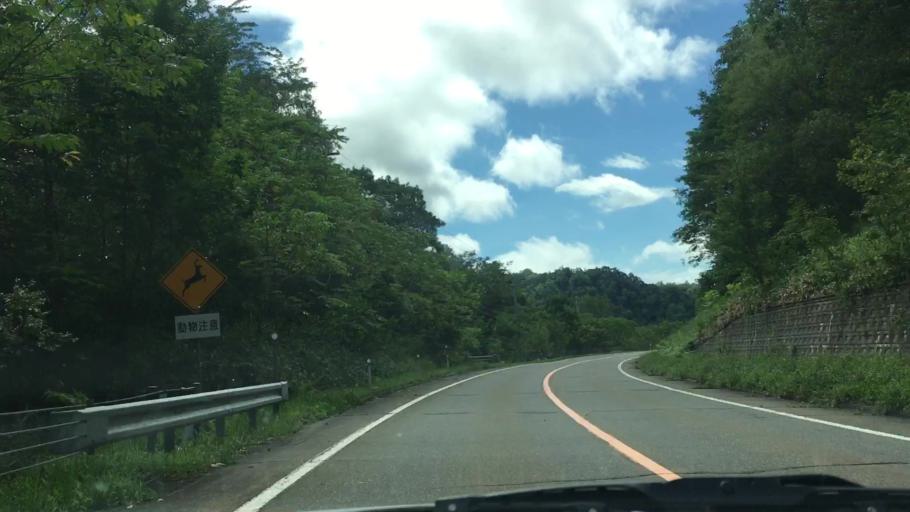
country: JP
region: Hokkaido
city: Kitami
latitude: 43.3488
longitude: 143.7769
